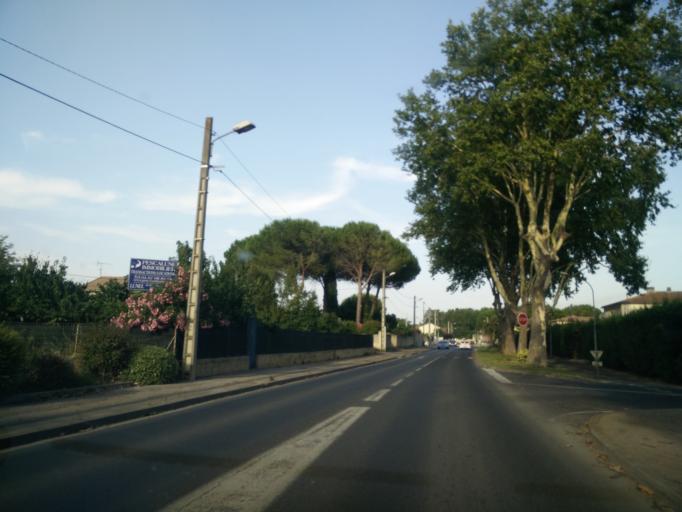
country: FR
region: Languedoc-Roussillon
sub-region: Departement de l'Herault
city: Marsillargues
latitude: 43.6632
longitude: 4.1692
